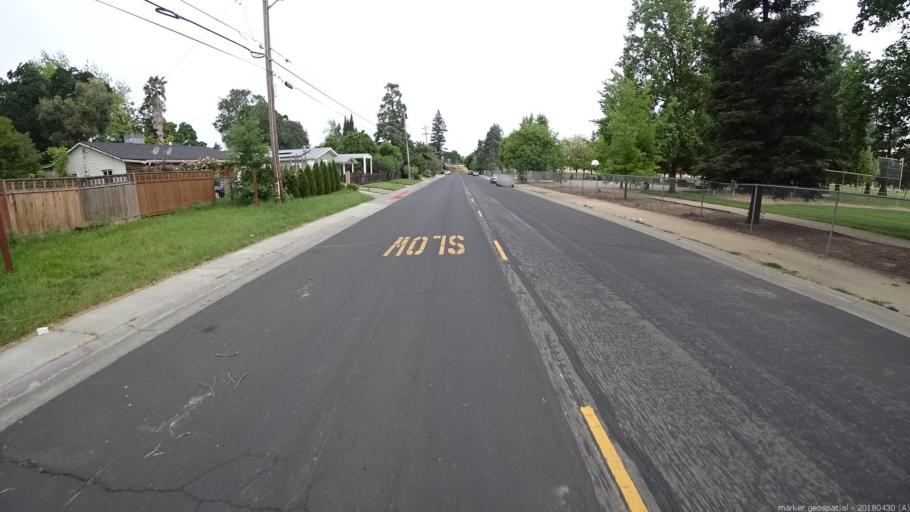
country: US
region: California
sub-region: Yolo County
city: West Sacramento
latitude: 38.5990
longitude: -121.5352
